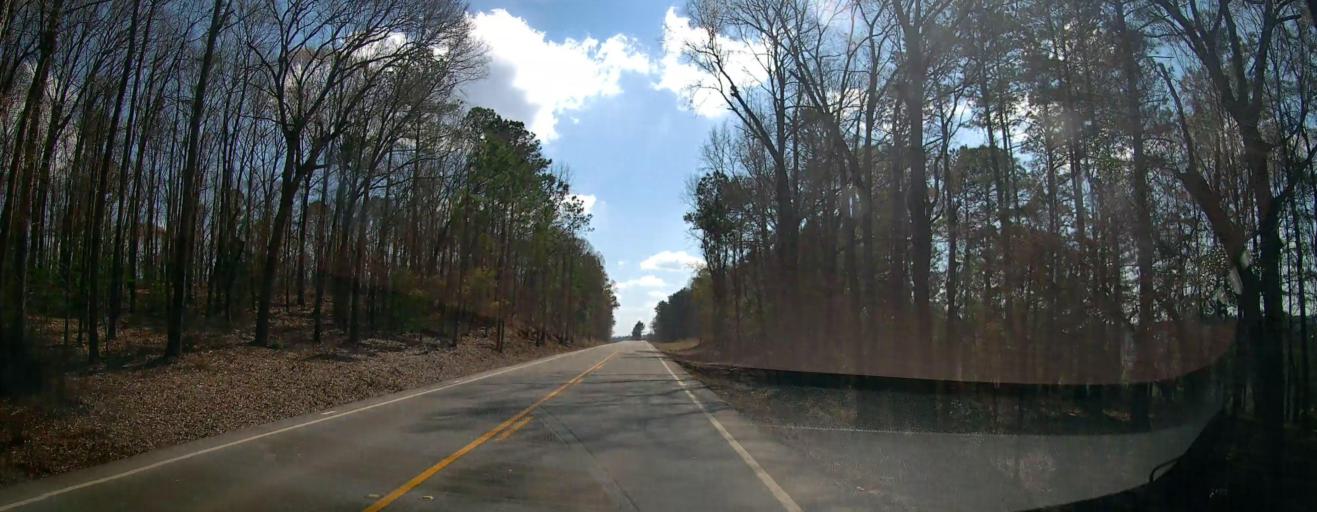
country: US
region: Georgia
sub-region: Wilkinson County
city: Gordon
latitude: 32.8073
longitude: -83.3256
